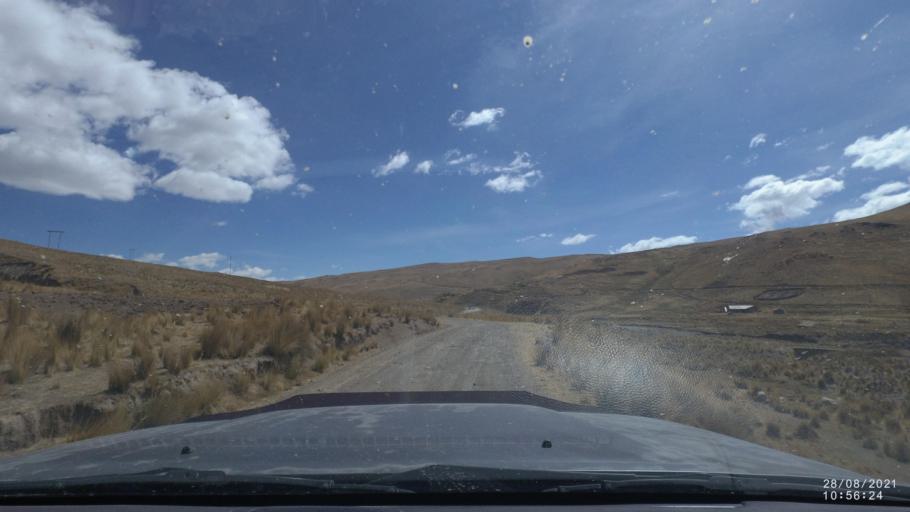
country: BO
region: Cochabamba
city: Cochabamba
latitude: -17.1933
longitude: -66.2497
